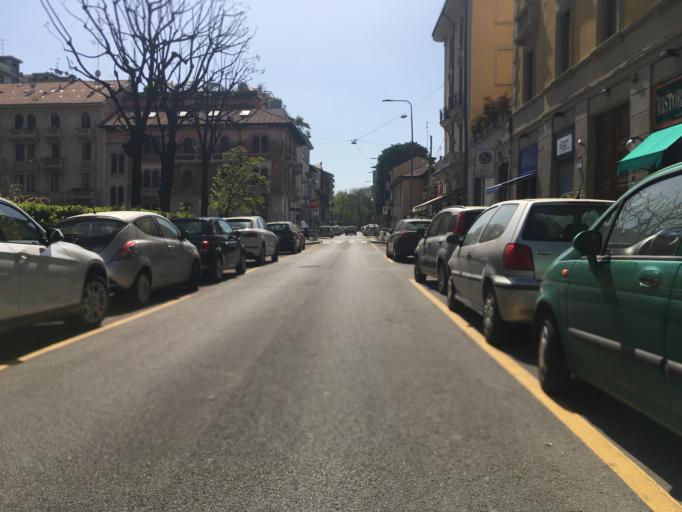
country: IT
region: Lombardy
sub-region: Citta metropolitana di Milano
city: Milano
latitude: 45.4738
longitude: 9.1485
